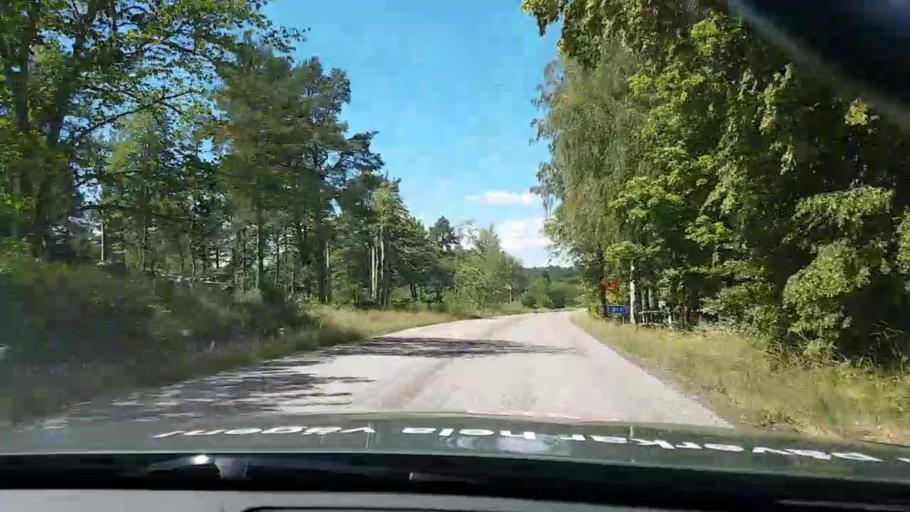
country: SE
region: Kalmar
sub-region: Vasterviks Kommun
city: Forserum
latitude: 57.9384
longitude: 16.4614
